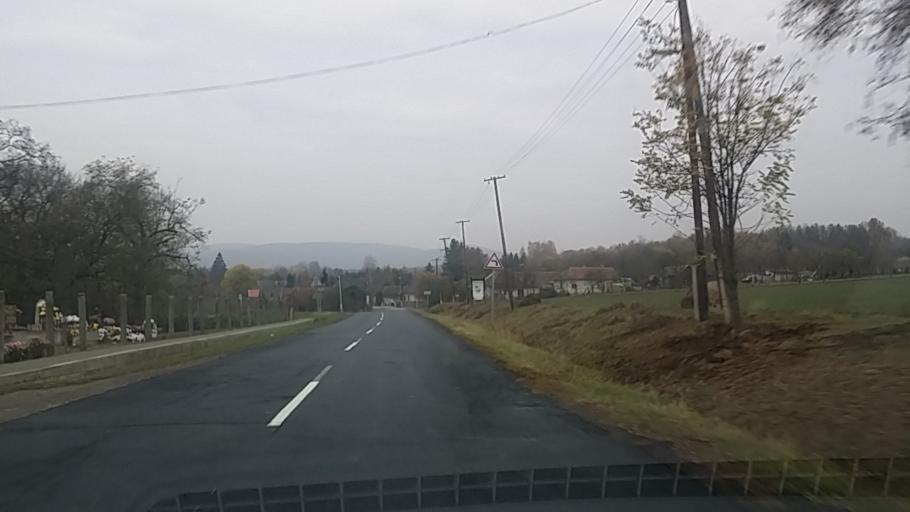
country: HU
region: Borsod-Abauj-Zemplen
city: Sarospatak
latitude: 48.4724
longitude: 21.4749
